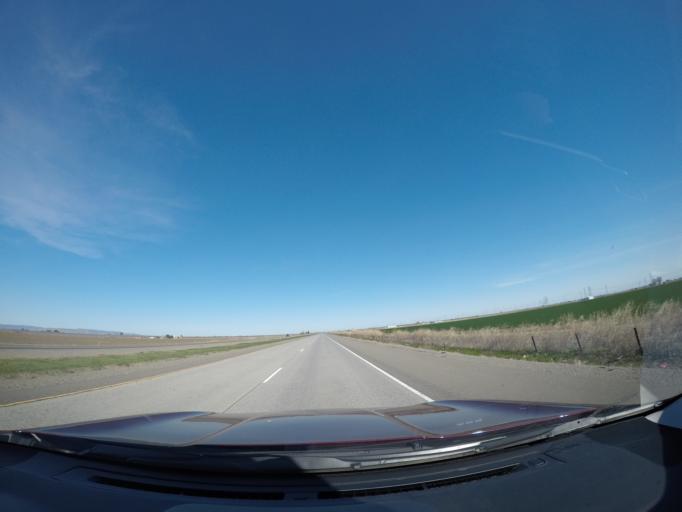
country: US
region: California
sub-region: Yolo County
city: Cottonwood
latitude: 38.6445
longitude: -121.9519
